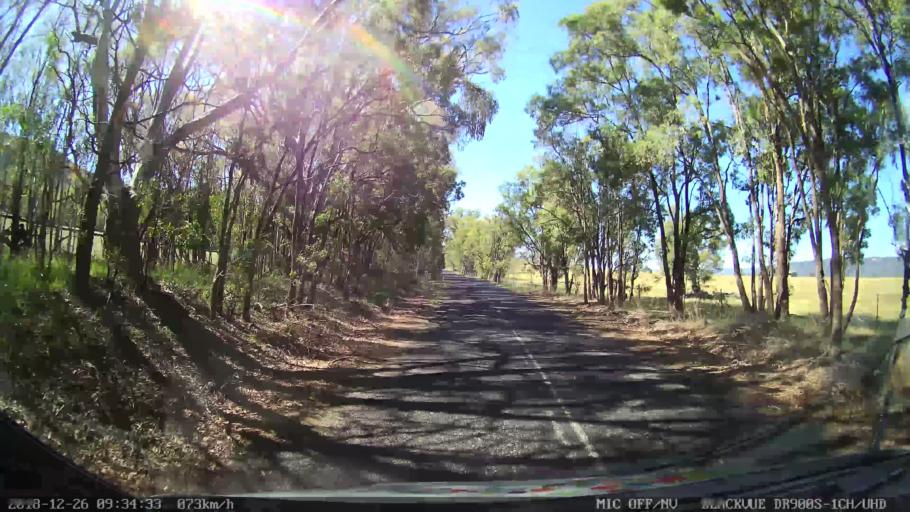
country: AU
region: New South Wales
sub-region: Mid-Western Regional
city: Kandos
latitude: -32.9064
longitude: 150.0378
